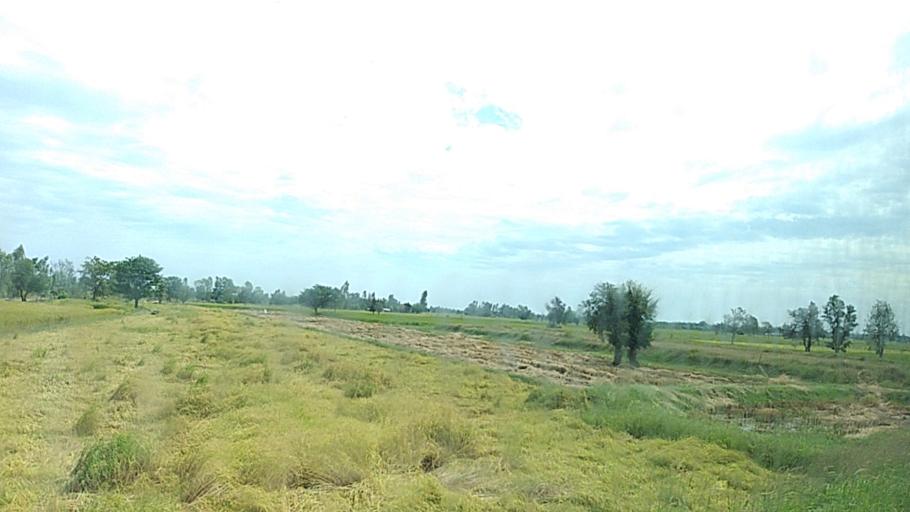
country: TH
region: Maha Sarakham
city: Chiang Yuen
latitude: 16.3767
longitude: 103.1044
